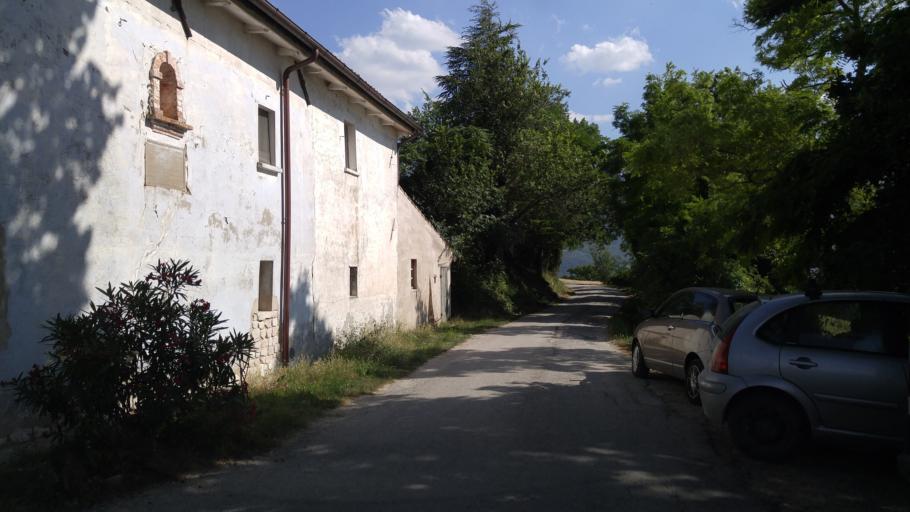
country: IT
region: The Marches
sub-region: Provincia di Pesaro e Urbino
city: Canavaccio
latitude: 43.6925
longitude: 12.7322
